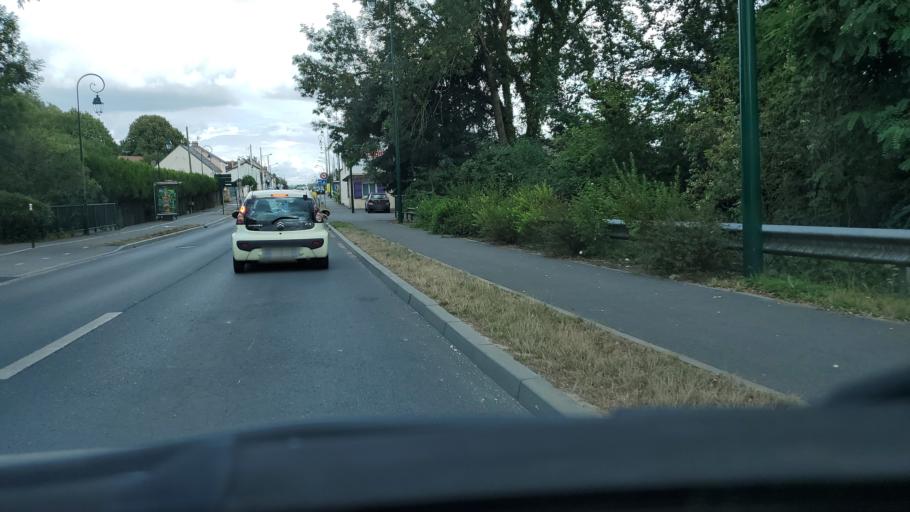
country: FR
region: Ile-de-France
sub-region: Departement de Seine-et-Marne
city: Mouroux
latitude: 48.8232
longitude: 3.0424
